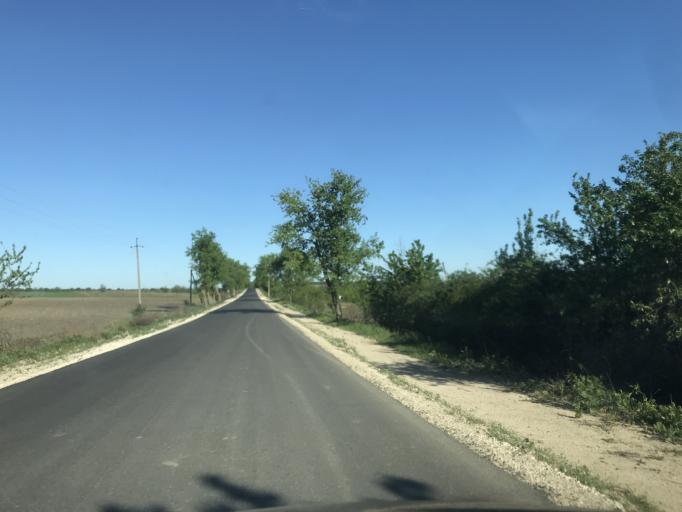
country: MD
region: Chisinau
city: Cricova
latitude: 47.2497
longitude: 28.8165
